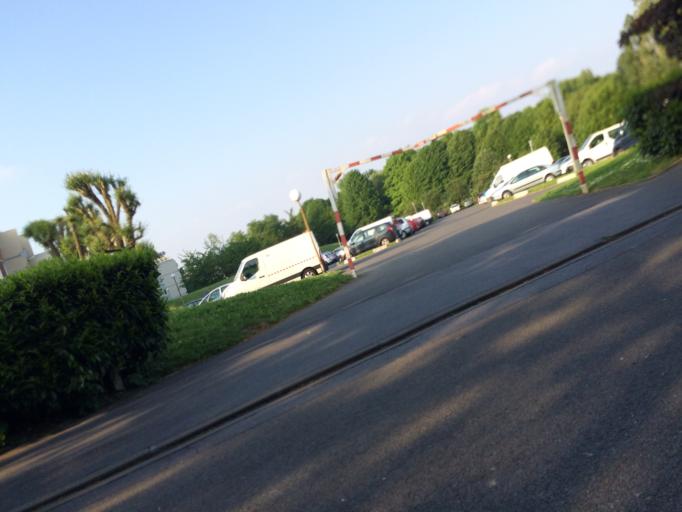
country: FR
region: Ile-de-France
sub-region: Departement de l'Essonne
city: Villebon-sur-Yvette
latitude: 48.7221
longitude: 2.2309
